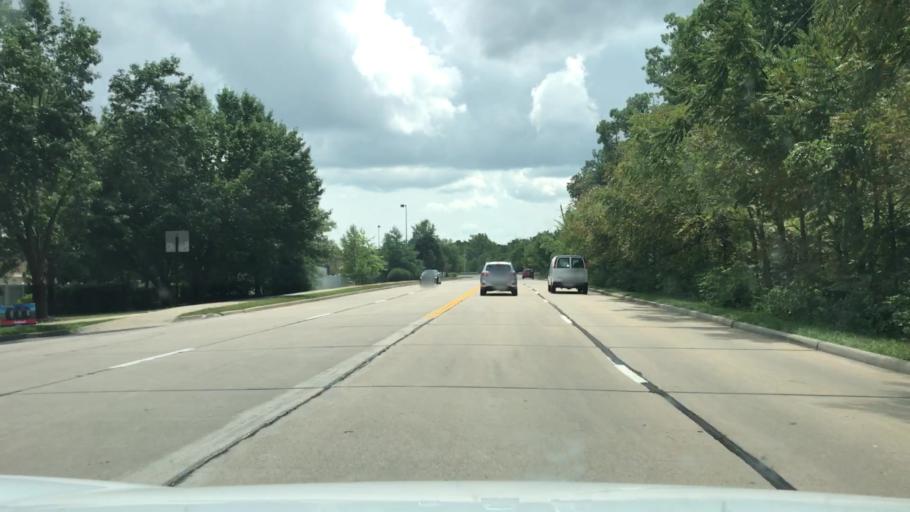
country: US
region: Missouri
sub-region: Saint Charles County
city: O'Fallon
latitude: 38.7954
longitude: -90.7036
